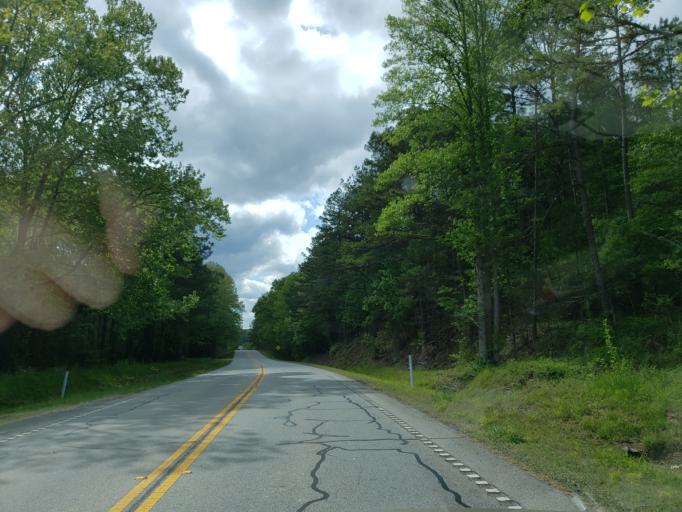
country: US
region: Georgia
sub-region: Haralson County
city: Tallapoosa
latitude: 33.7446
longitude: -85.3426
